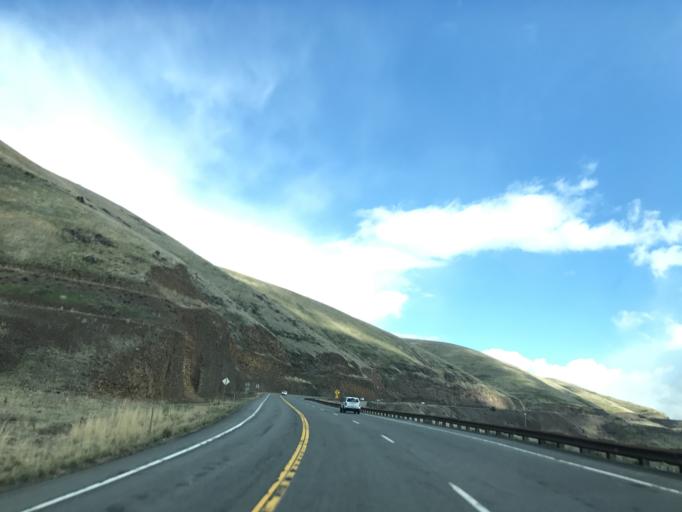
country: US
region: Idaho
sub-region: Idaho County
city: Grangeville
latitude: 45.8122
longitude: -116.2785
